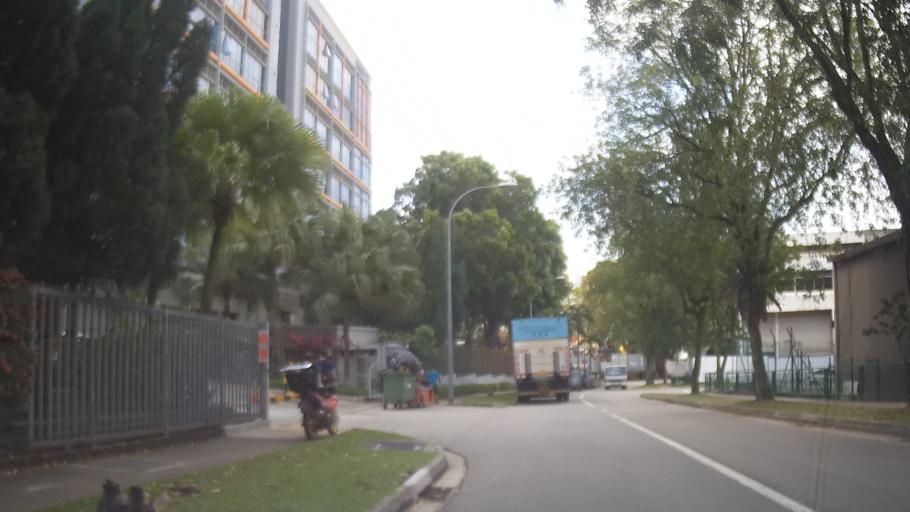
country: MY
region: Johor
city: Johor Bahru
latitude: 1.4056
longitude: 103.7583
